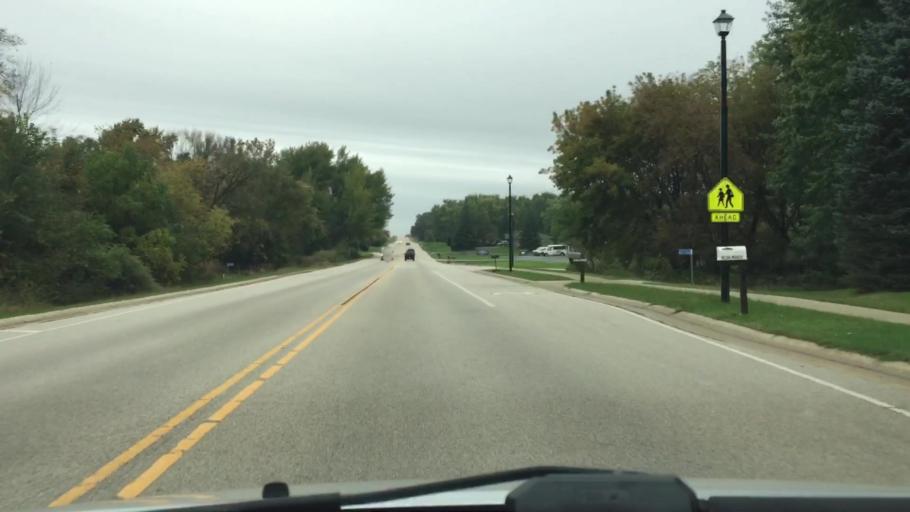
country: US
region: Wisconsin
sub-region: Waukesha County
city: Oconomowoc
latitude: 43.1302
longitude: -88.4998
